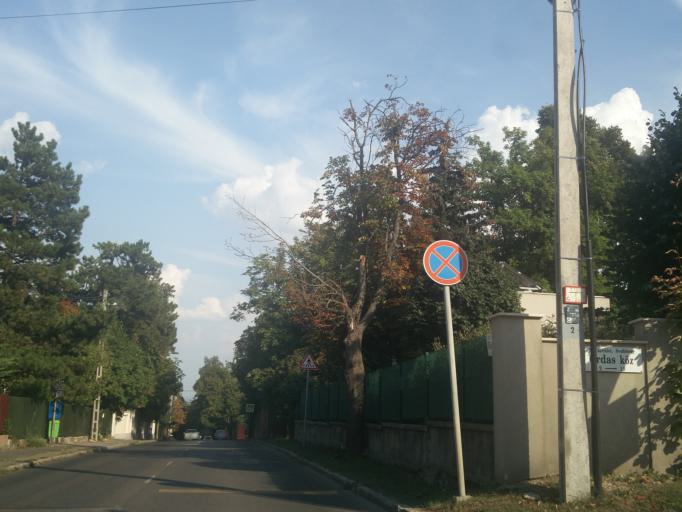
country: HU
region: Budapest
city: Budapest XII. keruelet
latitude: 47.4985
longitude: 18.9801
